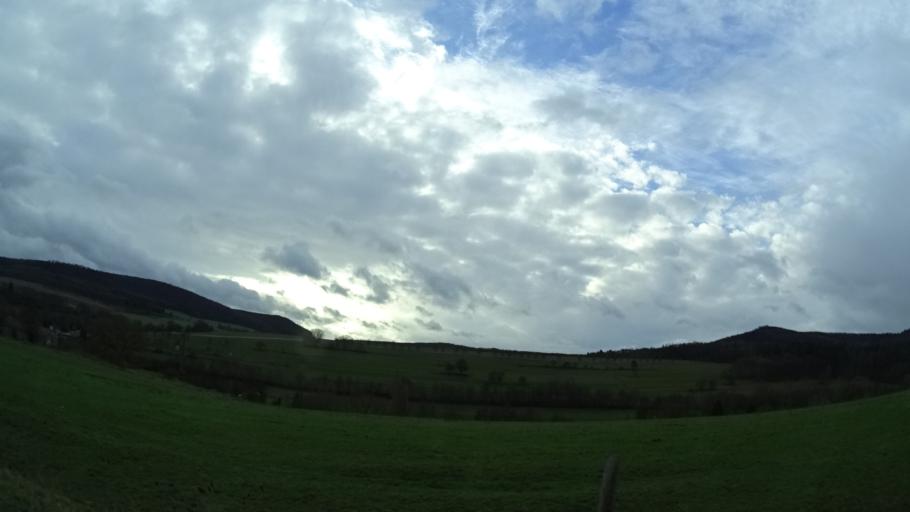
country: DE
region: Thuringia
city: Stepfershausen
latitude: 50.5583
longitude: 10.2782
